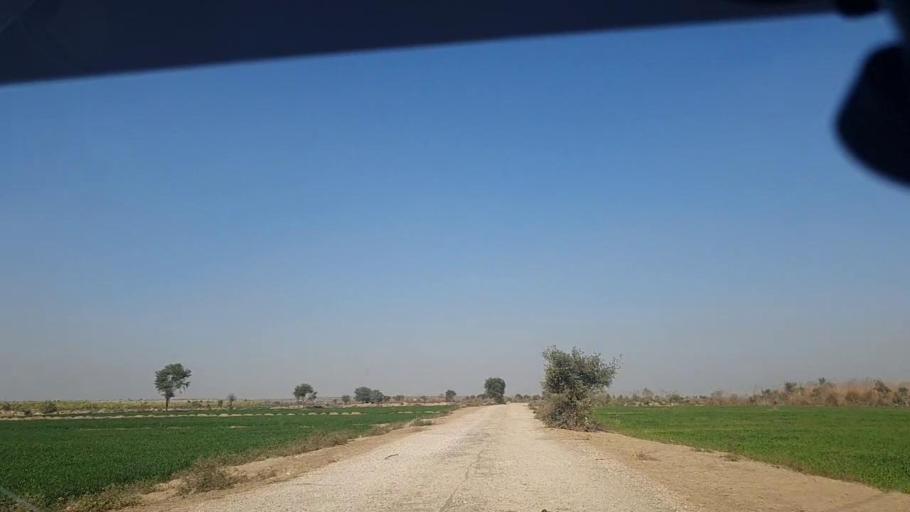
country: PK
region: Sindh
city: Khanpur
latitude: 27.5595
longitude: 69.3353
